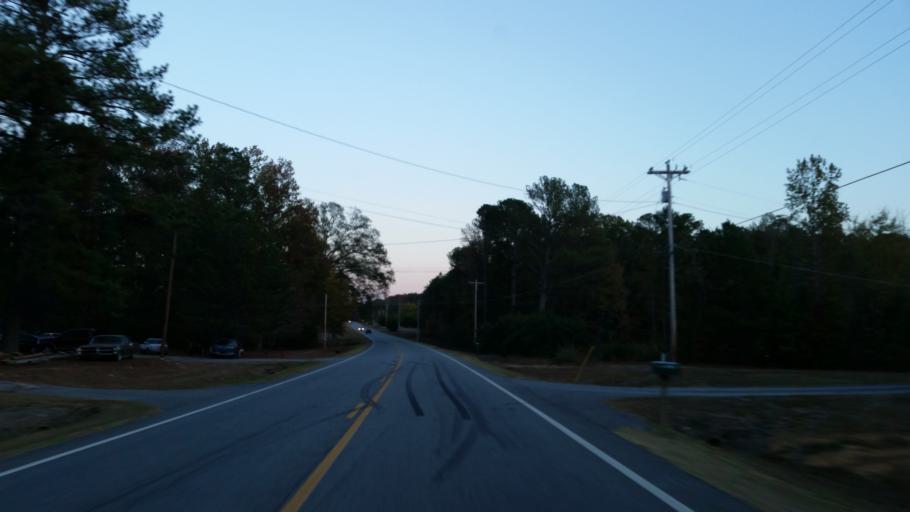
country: US
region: Georgia
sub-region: Gordon County
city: Calhoun
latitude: 34.5745
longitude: -84.9854
